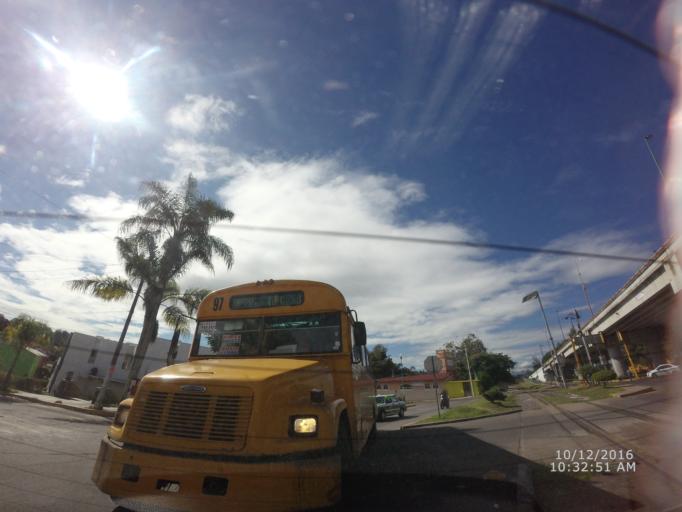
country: TR
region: Sivas
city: Karayun
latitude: 39.6712
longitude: 37.2567
